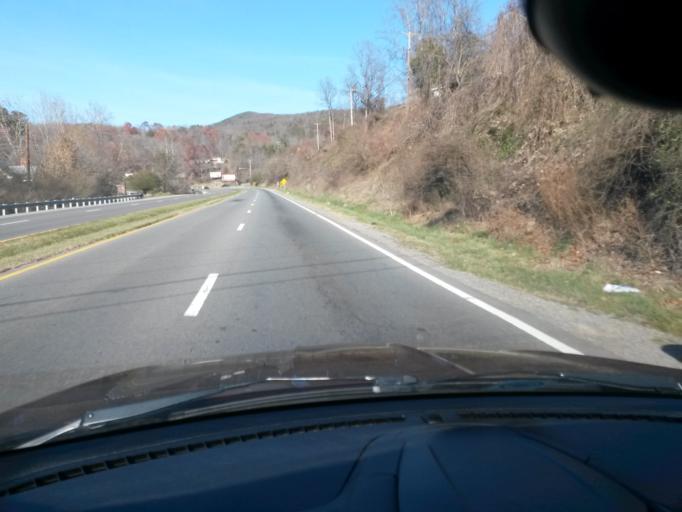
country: US
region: Virginia
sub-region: Roanoke County
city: Narrows
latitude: 37.1883
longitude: -79.9362
